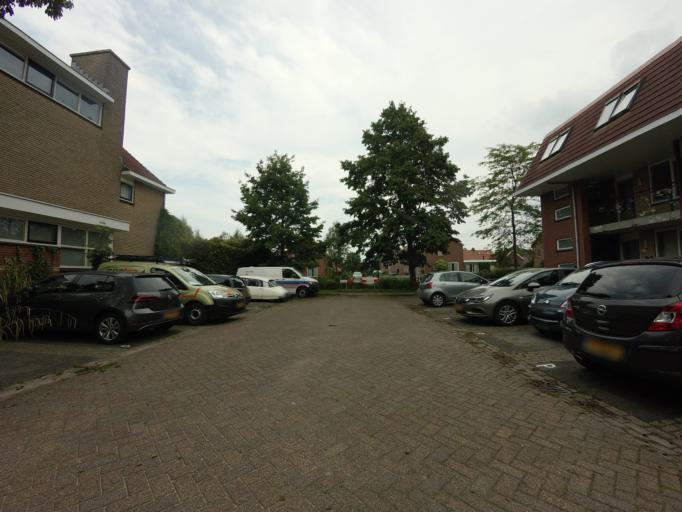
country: NL
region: Utrecht
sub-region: Stichtse Vecht
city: Breukelen
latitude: 52.1496
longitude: 4.9552
